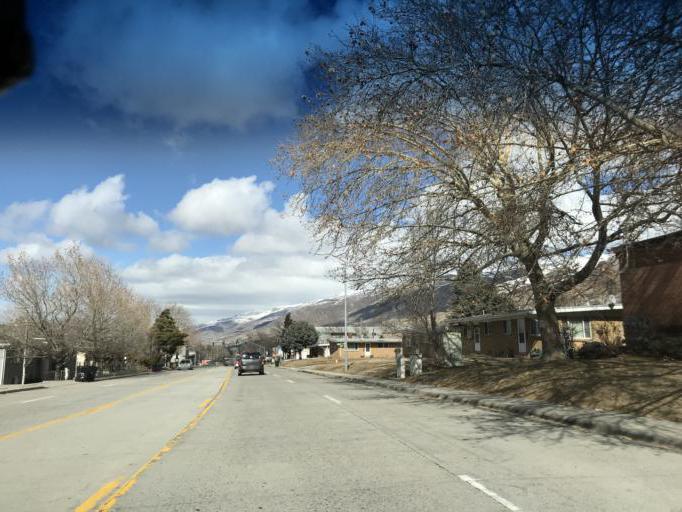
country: US
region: Utah
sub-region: Davis County
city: Bountiful
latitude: 40.8826
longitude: -111.8723
